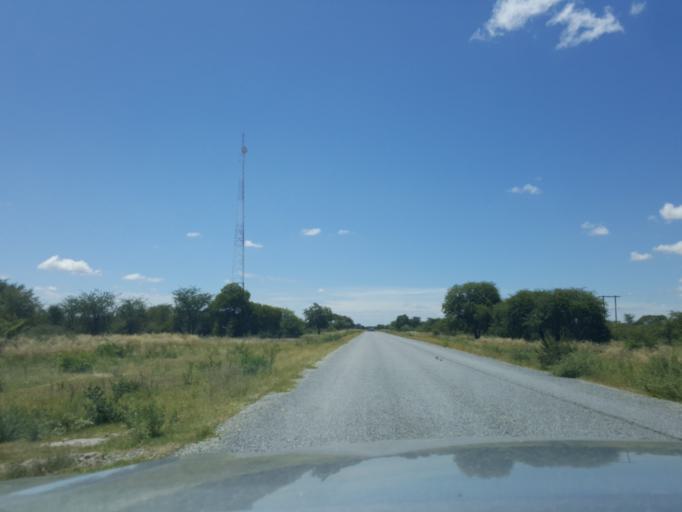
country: BW
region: Central
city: Nata
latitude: -20.1509
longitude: 25.7666
